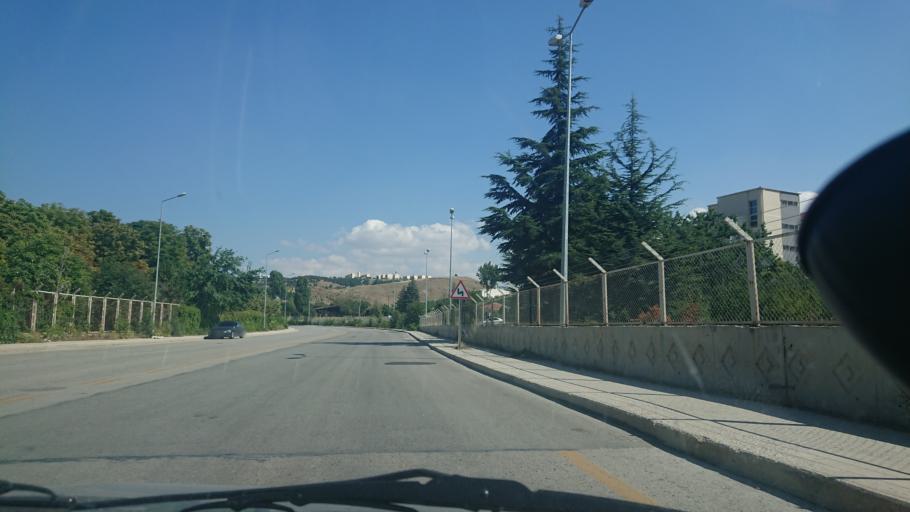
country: TR
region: Ankara
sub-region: Goelbasi
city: Golbasi
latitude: 39.8071
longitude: 32.8188
